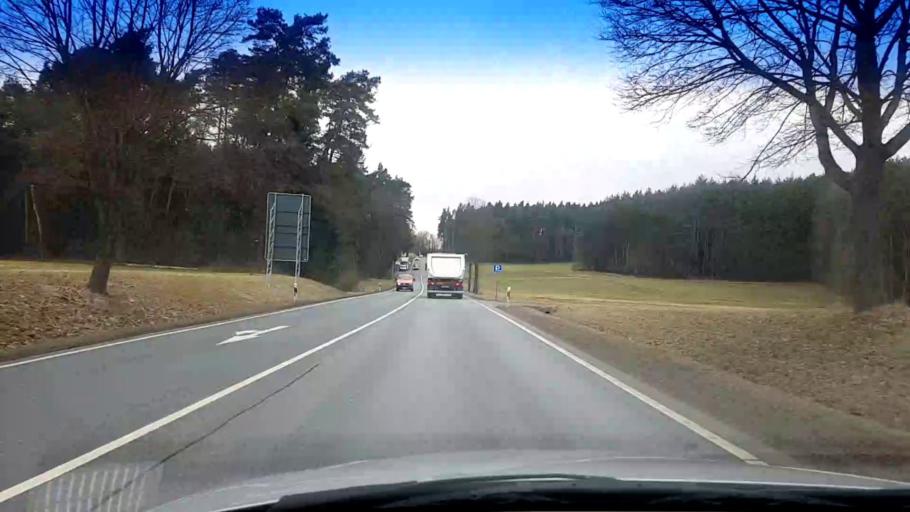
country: DE
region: Bavaria
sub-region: Upper Franconia
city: Neudrossenfeld
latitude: 50.0416
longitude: 11.4887
